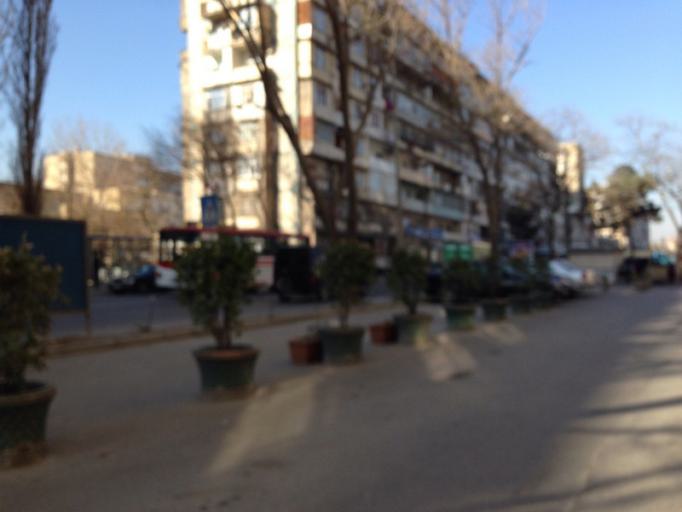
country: AZ
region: Baki
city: Baku
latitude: 40.4066
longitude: 49.8755
